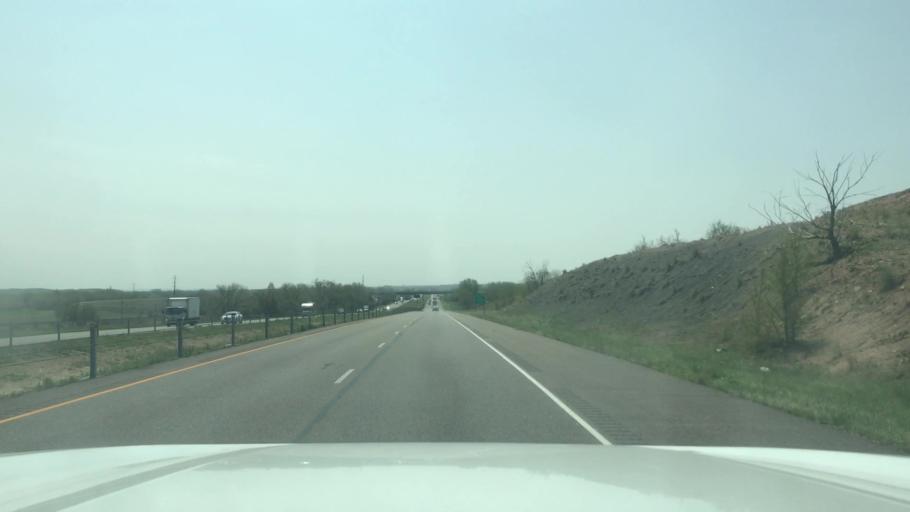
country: US
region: Colorado
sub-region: El Paso County
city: Fountain
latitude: 38.6433
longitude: -104.6940
